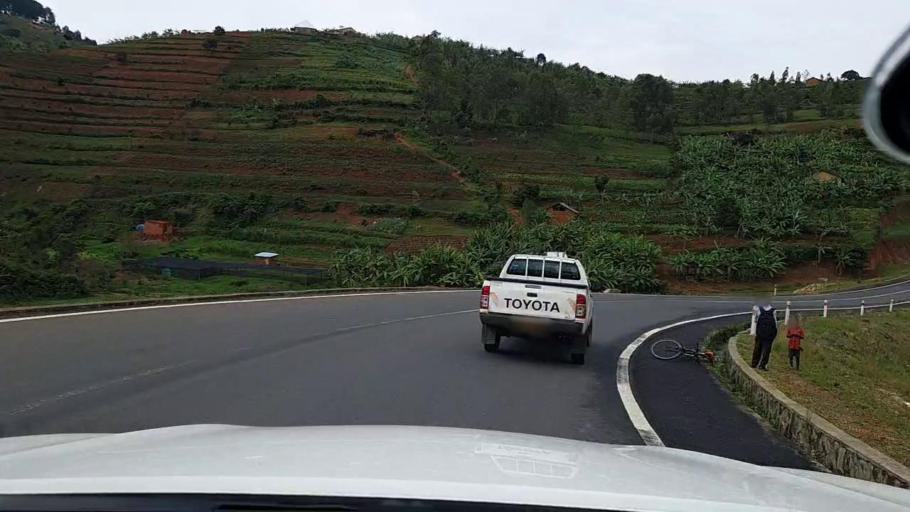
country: RW
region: Western Province
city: Kibuye
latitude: -2.1663
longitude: 29.2969
